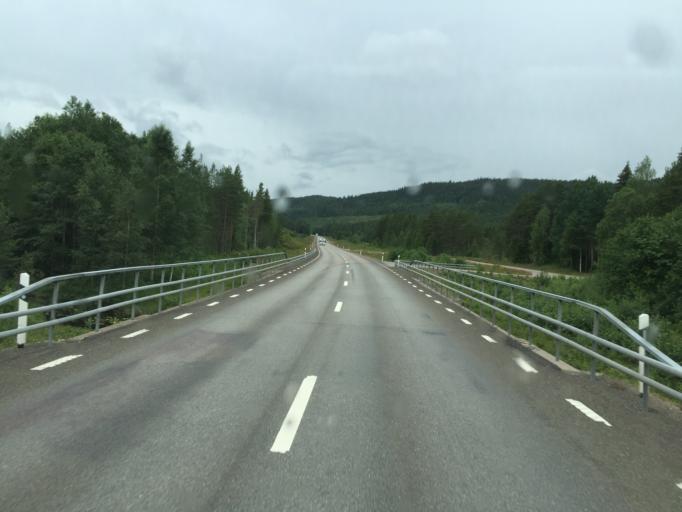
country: SE
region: Dalarna
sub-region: Malung-Saelens kommun
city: Malung
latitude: 60.6449
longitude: 13.6273
